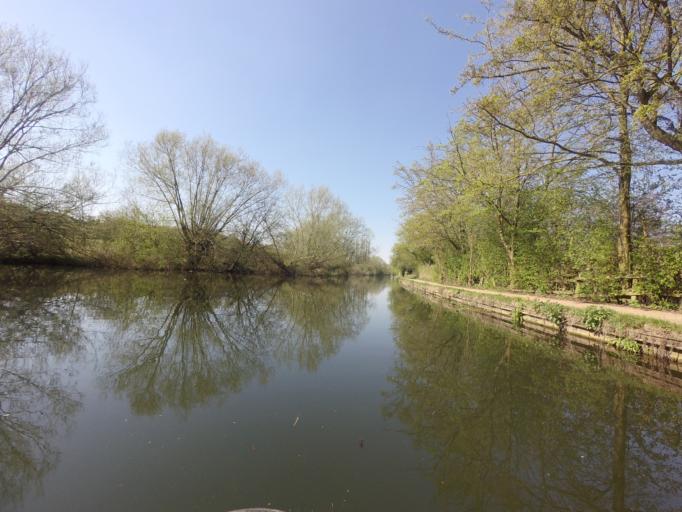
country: GB
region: England
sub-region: Hertfordshire
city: Kings Langley
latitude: 51.7194
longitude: -0.4483
